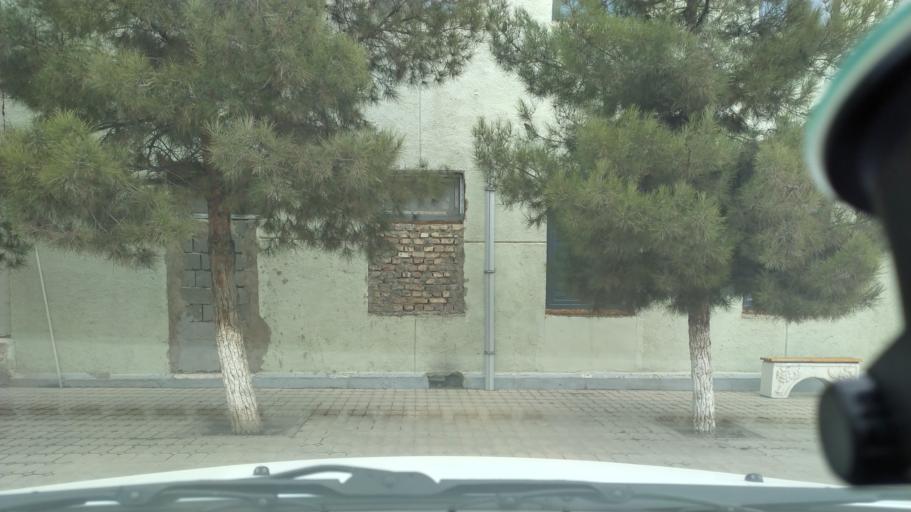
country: UZ
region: Namangan
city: Namangan Shahri
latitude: 41.0099
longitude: 71.6476
